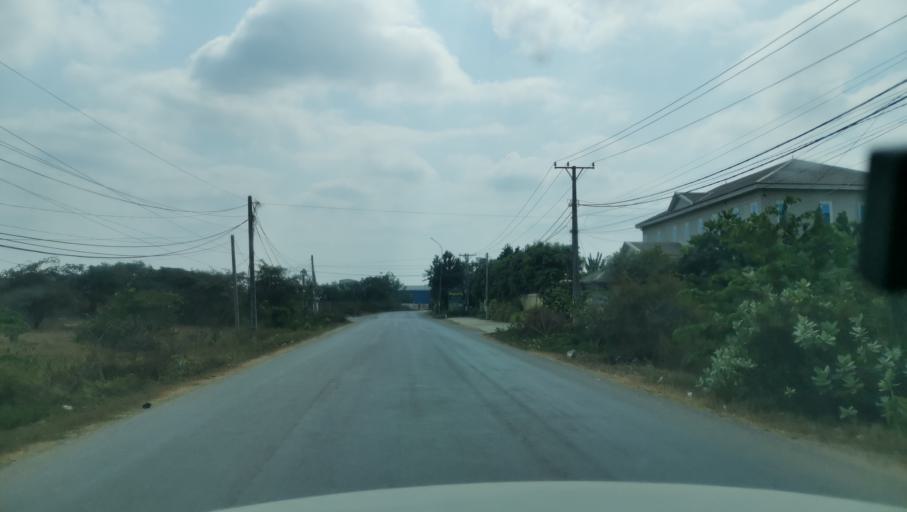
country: KH
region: Battambang
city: Battambang
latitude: 13.0793
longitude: 103.1860
